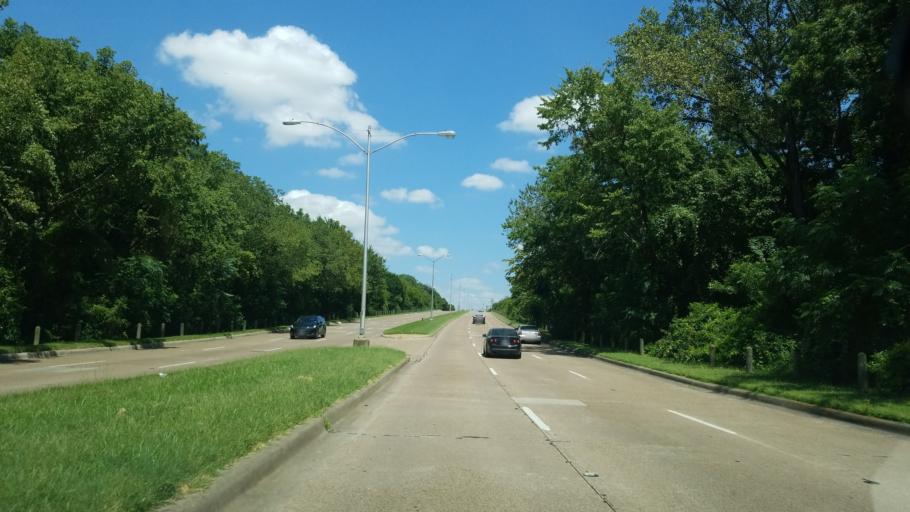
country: US
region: Texas
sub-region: Dallas County
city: Balch Springs
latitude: 32.7492
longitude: -96.7079
